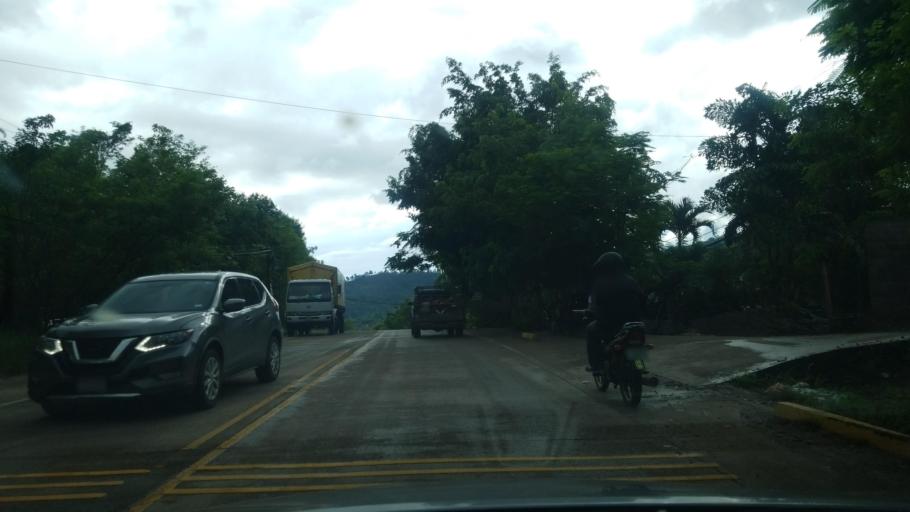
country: HN
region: Copan
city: Copan
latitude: 14.8422
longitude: -89.1668
